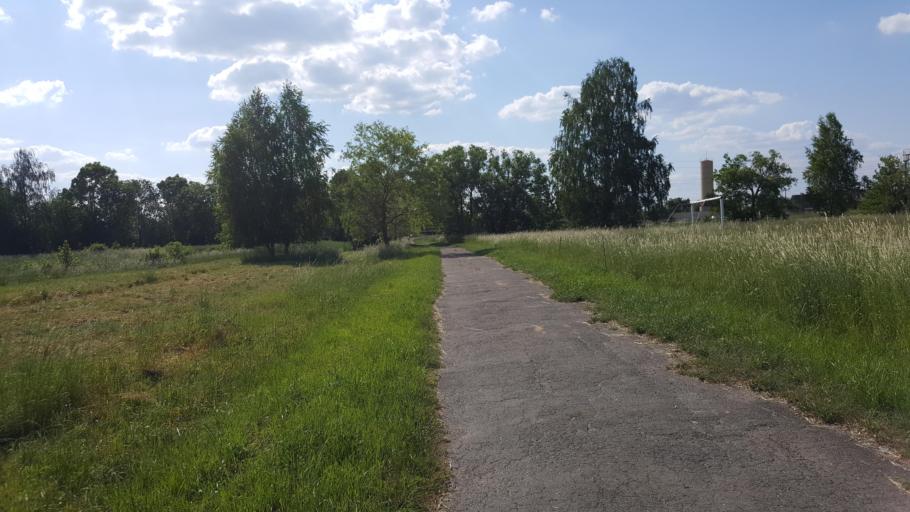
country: BY
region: Brest
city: Kobryn
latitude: 52.3400
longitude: 24.2389
